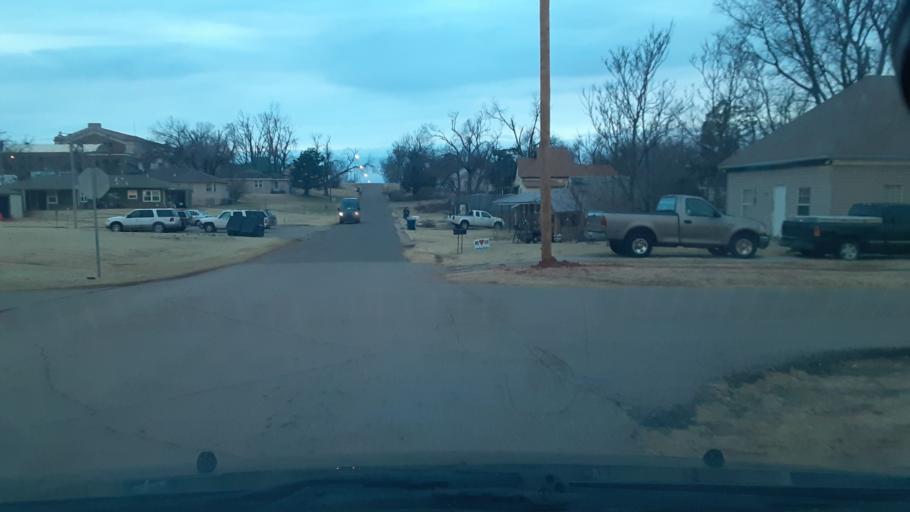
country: US
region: Oklahoma
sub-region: Logan County
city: Guthrie
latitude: 35.8792
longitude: -97.4098
